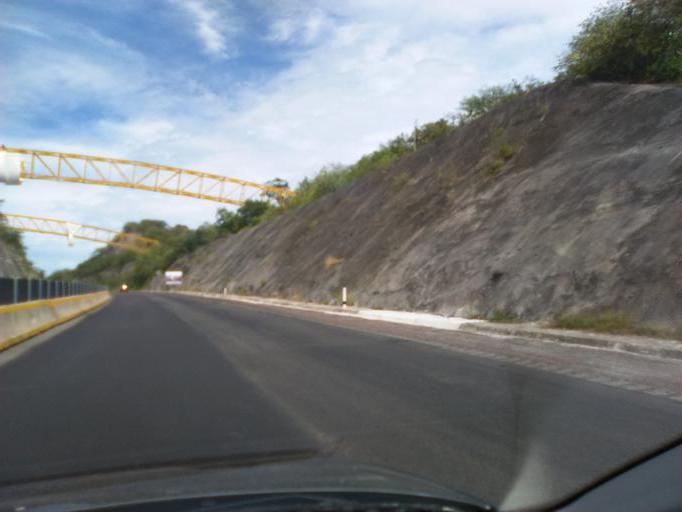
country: MX
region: Guerrero
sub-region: Chilpancingo de los Bravo
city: Acahuizotla
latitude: 17.3853
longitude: -99.4709
